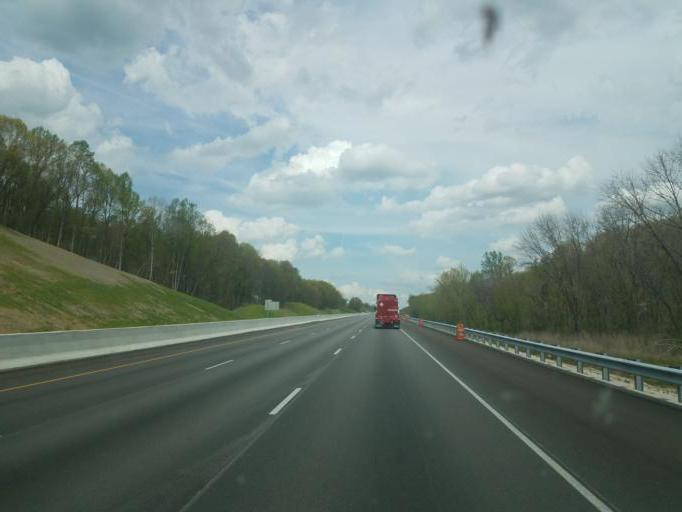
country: US
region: Kentucky
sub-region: Hart County
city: Munfordville
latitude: 37.3118
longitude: -85.9040
